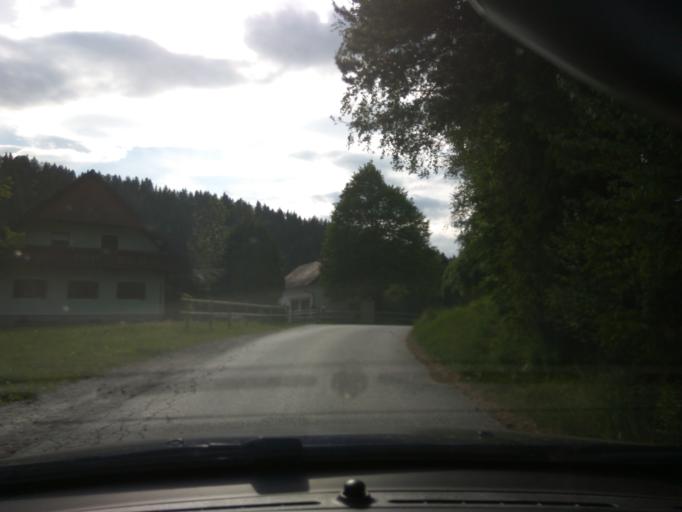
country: AT
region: Styria
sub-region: Politischer Bezirk Voitsberg
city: Voitsberg
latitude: 47.0305
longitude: 15.1151
